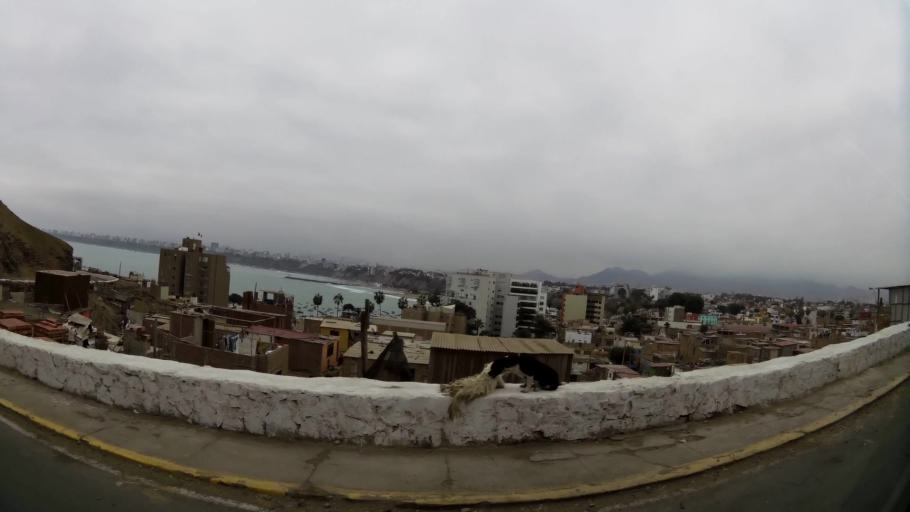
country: PE
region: Lima
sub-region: Lima
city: Surco
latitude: -12.1693
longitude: -77.0325
